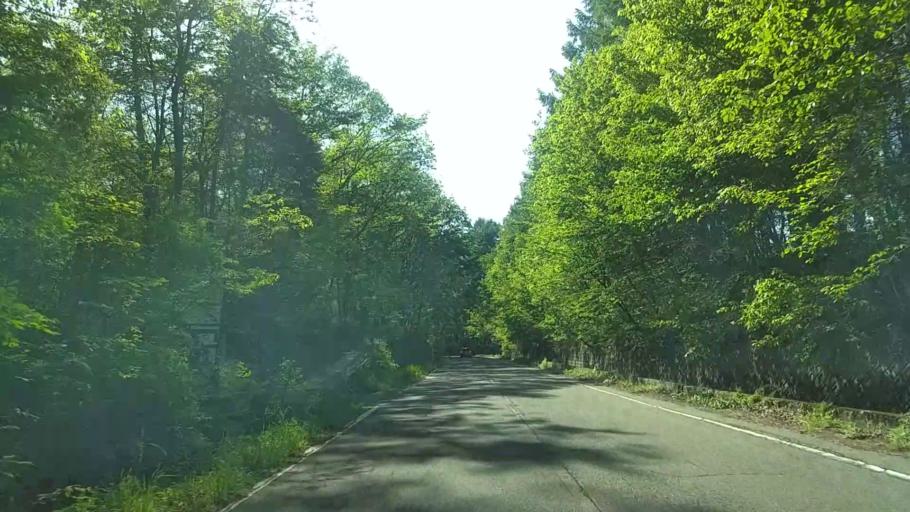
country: JP
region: Yamanashi
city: Nirasaki
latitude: 35.8897
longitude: 138.3548
